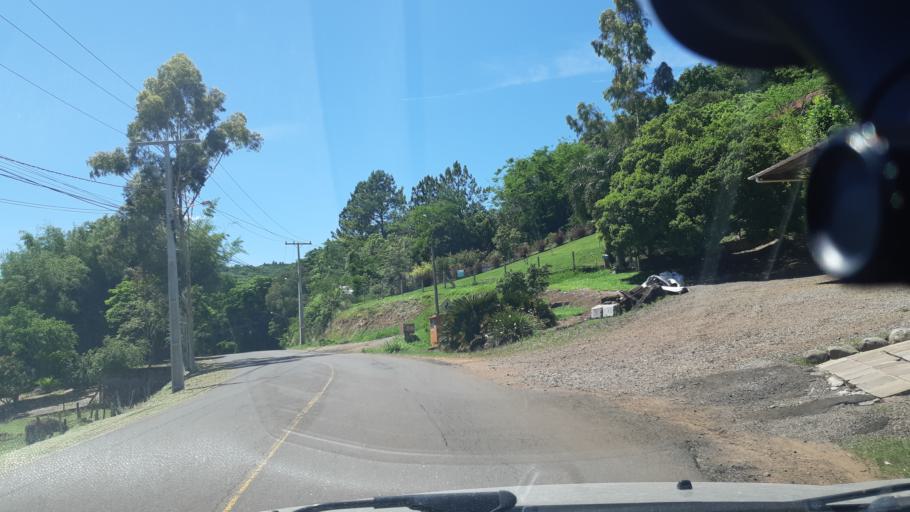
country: BR
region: Rio Grande do Sul
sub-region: Novo Hamburgo
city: Novo Hamburgo
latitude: -29.6259
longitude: -51.1000
